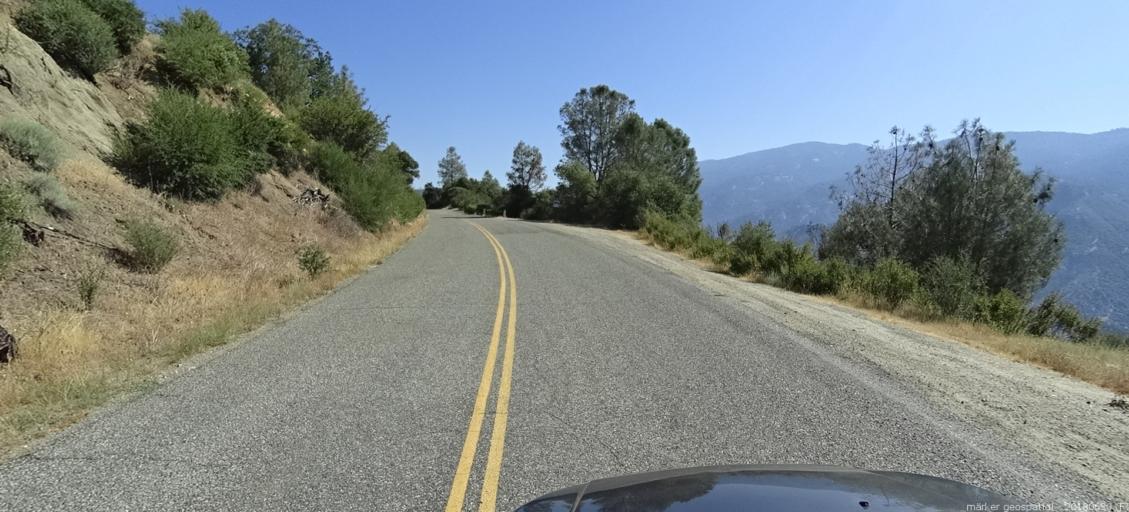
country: US
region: California
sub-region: Fresno County
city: Auberry
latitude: 37.2168
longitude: -119.3514
